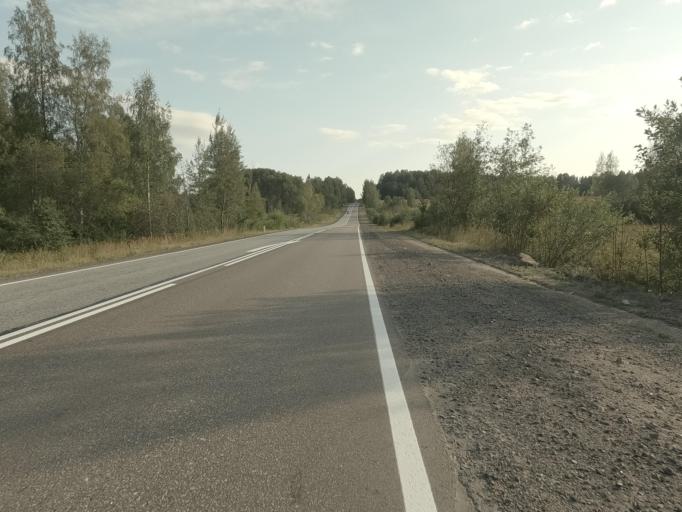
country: RU
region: Leningrad
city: Vyborg
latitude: 60.8394
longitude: 28.8401
